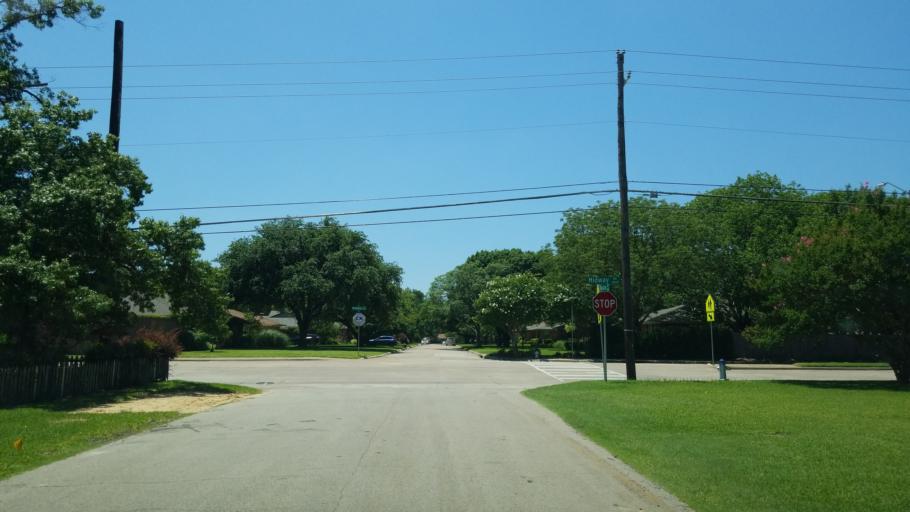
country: US
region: Texas
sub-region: Dallas County
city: University Park
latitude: 32.8779
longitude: -96.8380
